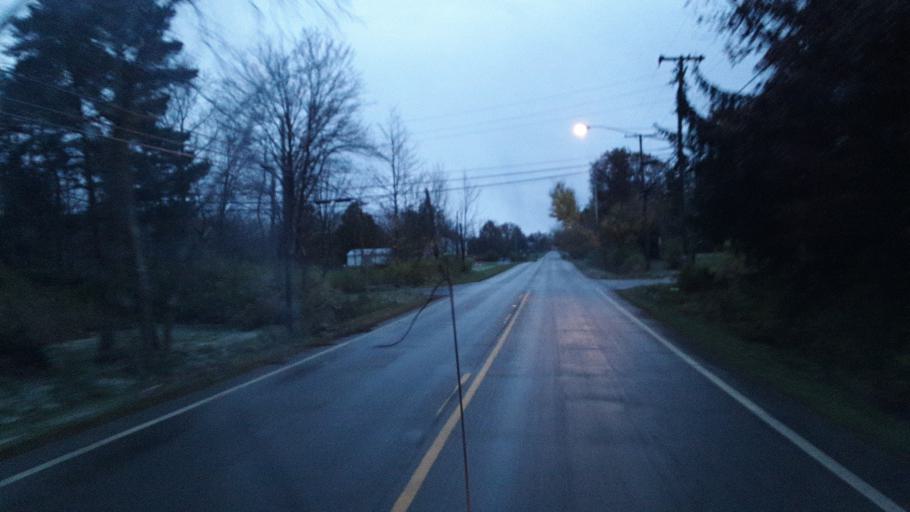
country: US
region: Ohio
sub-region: Portage County
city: Mantua
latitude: 41.3319
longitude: -81.2216
